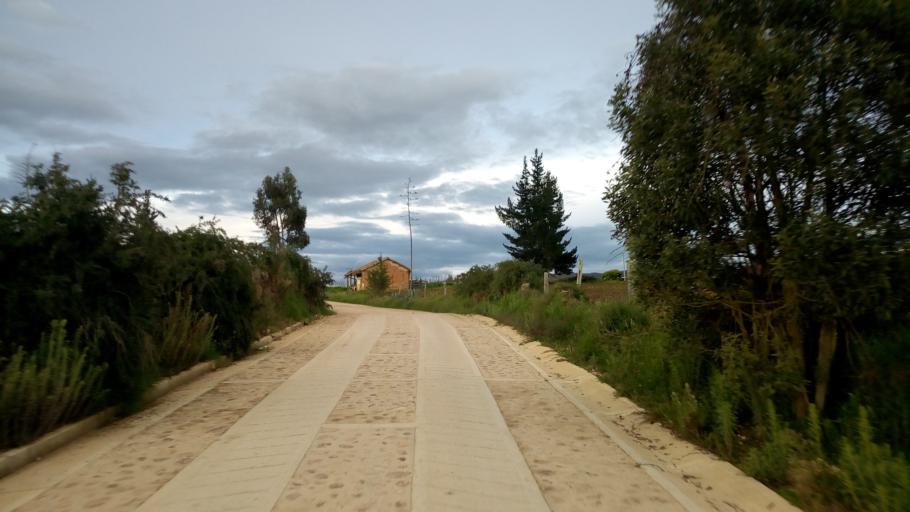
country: CO
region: Boyaca
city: Toca
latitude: 5.5837
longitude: -73.1721
